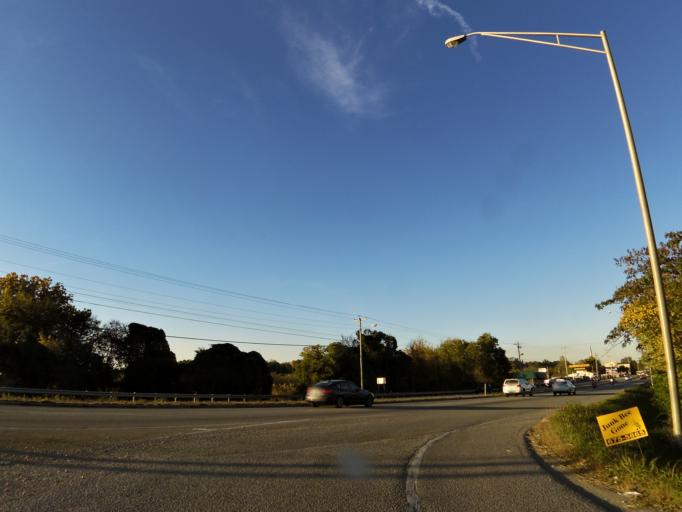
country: US
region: Tennessee
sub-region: Blount County
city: Alcoa
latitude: 35.8479
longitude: -83.9645
